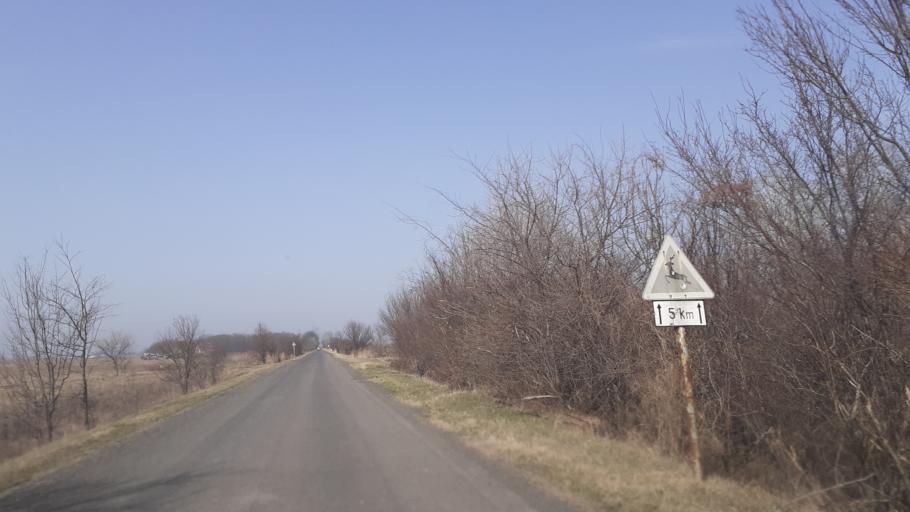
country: HU
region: Pest
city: Dabas
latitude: 47.1158
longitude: 19.2175
